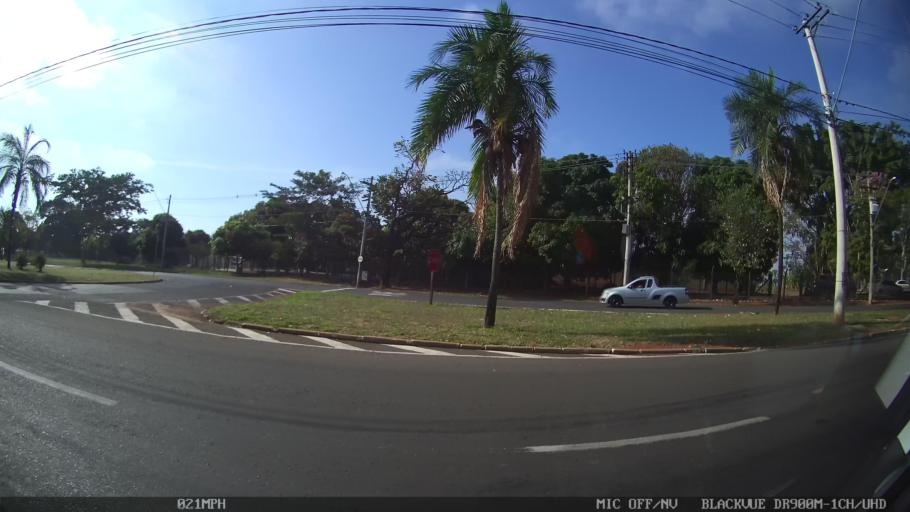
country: BR
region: Sao Paulo
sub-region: Sao Jose Do Rio Preto
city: Sao Jose do Rio Preto
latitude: -20.8163
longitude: -49.4110
